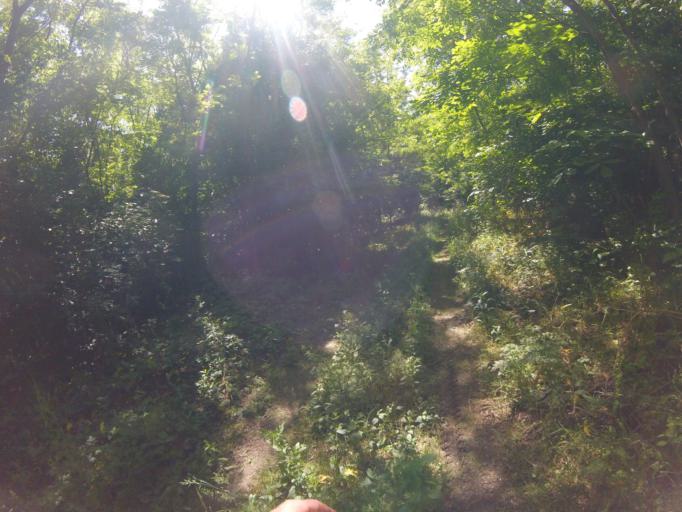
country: HU
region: Zala
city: Zalaszentgrot
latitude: 46.9154
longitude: 17.0424
